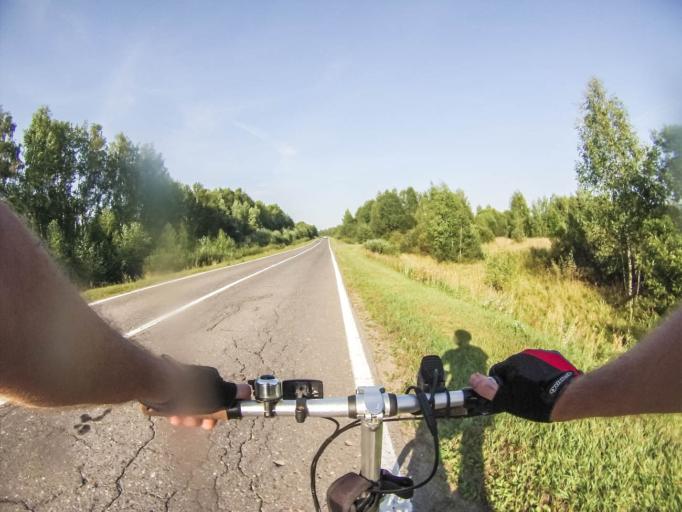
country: RU
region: Jaroslavl
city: Uglich
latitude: 57.6822
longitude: 38.3221
